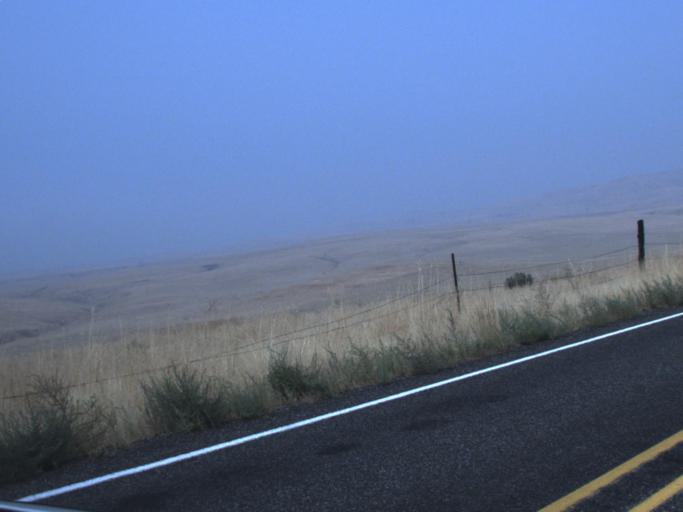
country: US
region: Washington
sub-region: Yakima County
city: Sunnyside
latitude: 46.4144
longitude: -119.9478
